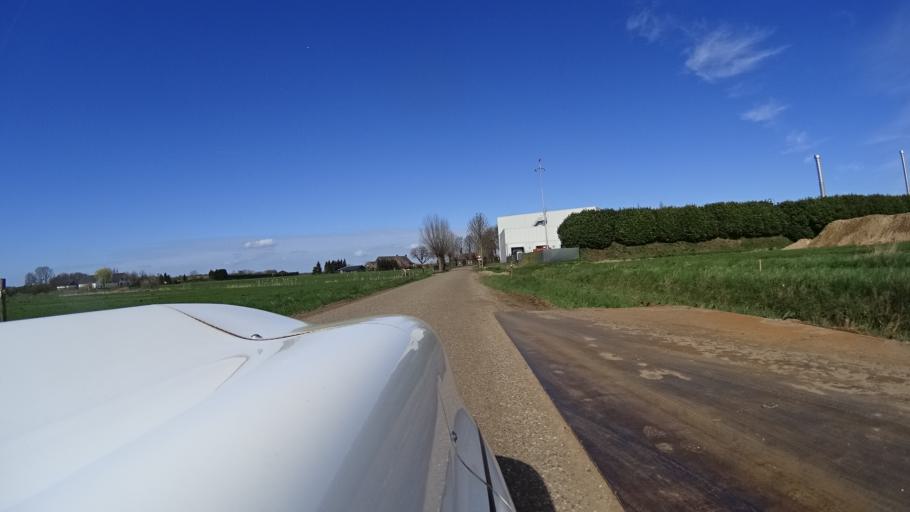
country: NL
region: Limburg
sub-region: Gemeente Bergen
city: Wellerlooi
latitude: 51.5062
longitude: 6.1497
